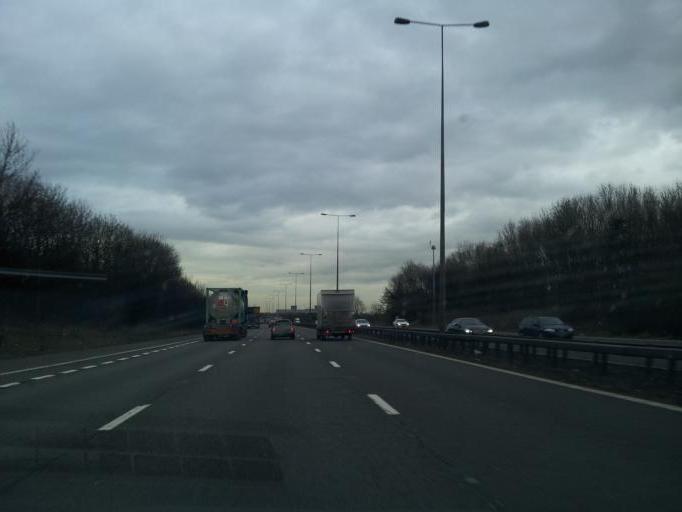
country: GB
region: England
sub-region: Warwickshire
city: Brandon
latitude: 52.4372
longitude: -1.4198
